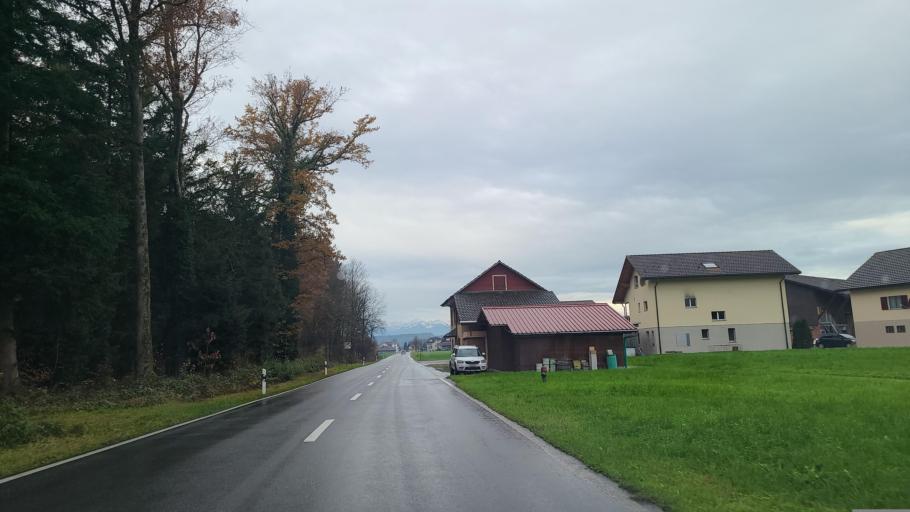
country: CH
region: Aargau
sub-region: Bezirk Muri
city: Sins
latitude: 47.2027
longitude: 8.4167
